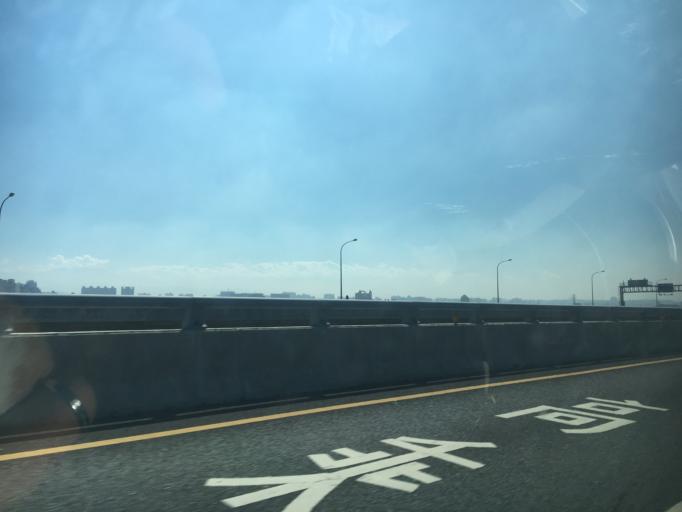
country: TW
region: Taiwan
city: Taoyuan City
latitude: 25.0287
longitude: 121.2844
